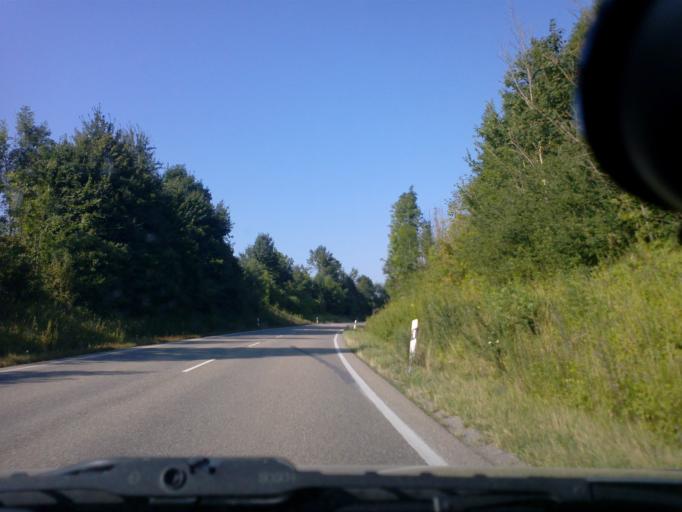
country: DE
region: Baden-Wuerttemberg
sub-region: Karlsruhe Region
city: Zaisenhausen
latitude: 49.1096
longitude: 8.8258
